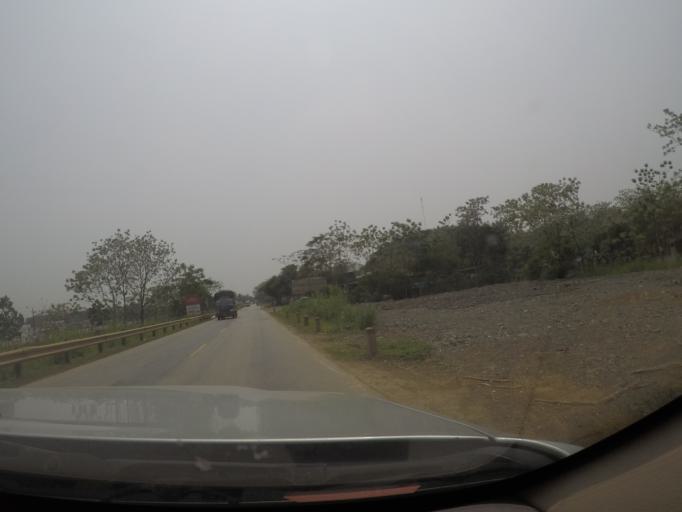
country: VN
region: Thanh Hoa
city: Thi Tran Thuong Xuan
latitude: 19.9890
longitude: 105.4047
